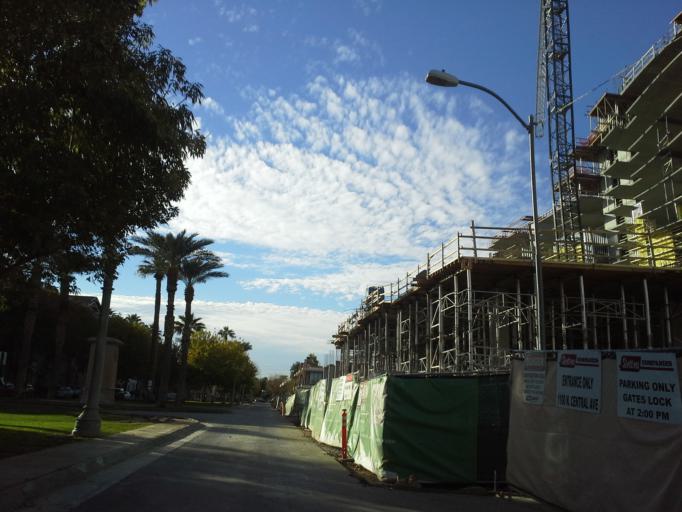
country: US
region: Arizona
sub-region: Maricopa County
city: Phoenix
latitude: 33.4600
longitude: -112.0748
